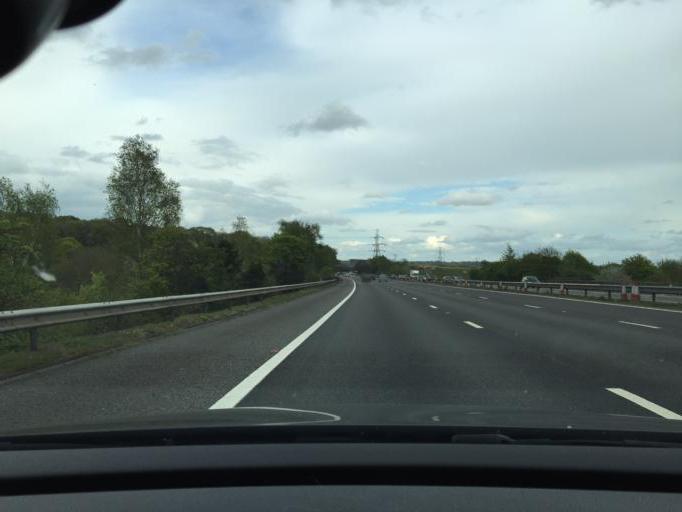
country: GB
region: England
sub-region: West Berkshire
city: Basildon
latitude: 51.4595
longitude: -1.1261
